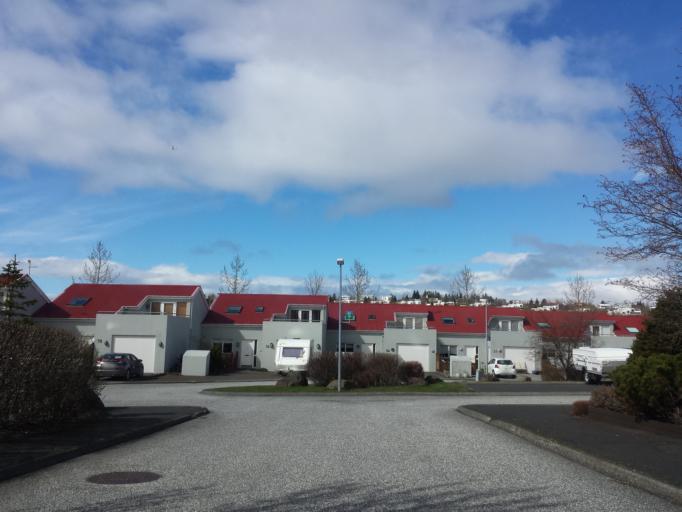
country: IS
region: Capital Region
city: Kopavogur
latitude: 64.1036
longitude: -21.8912
